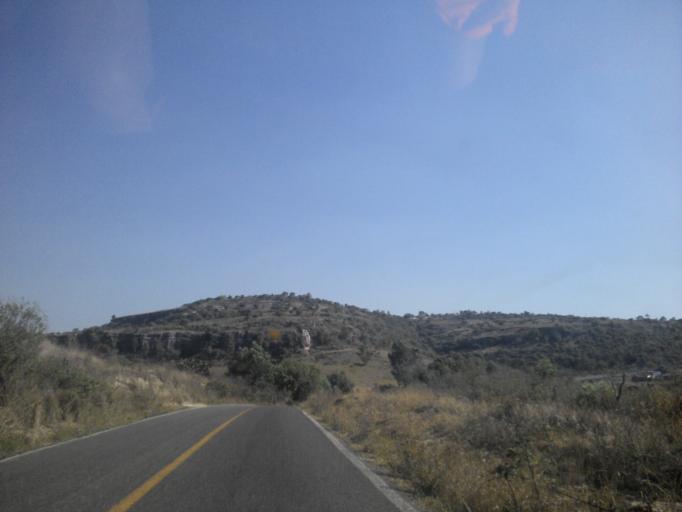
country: MX
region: Jalisco
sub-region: Arandas
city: Santiaguito (Santiaguito de Velazquez)
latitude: 20.7871
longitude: -102.2736
